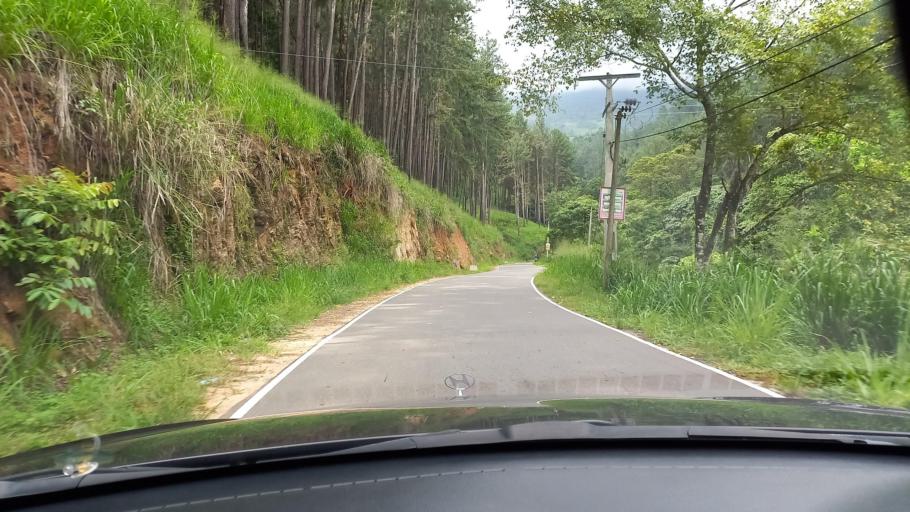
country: LK
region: Central
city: Gampola
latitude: 7.2126
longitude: 80.6189
